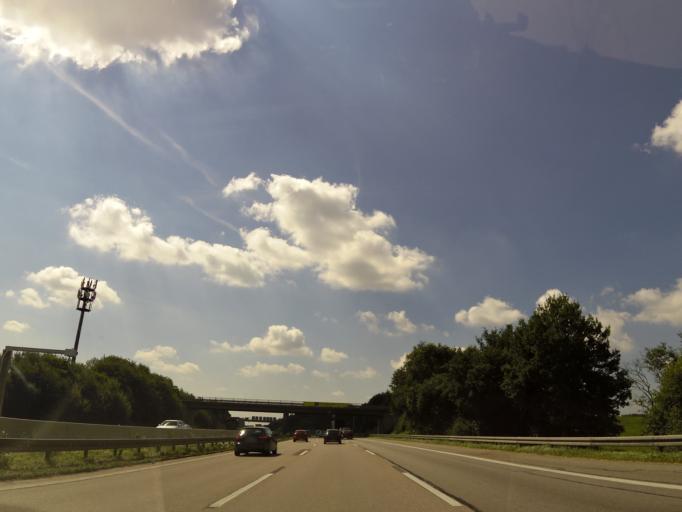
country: DE
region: Bavaria
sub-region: Upper Bavaria
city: Paunzhausen
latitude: 48.4750
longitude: 11.5850
